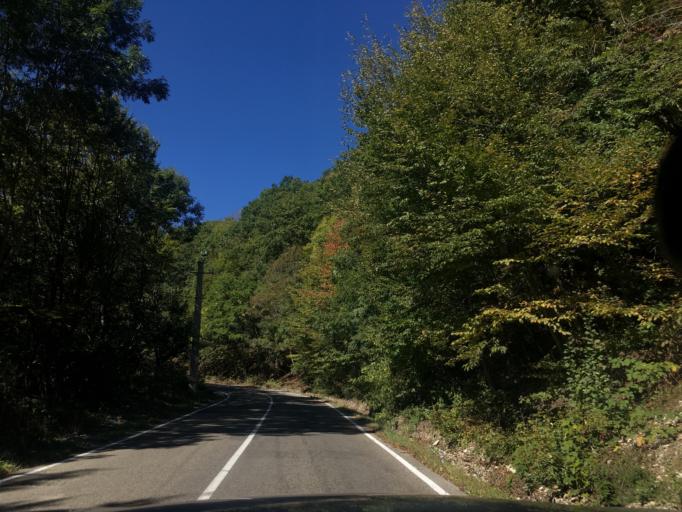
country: GE
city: Didi Lilo
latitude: 41.8709
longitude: 44.9152
